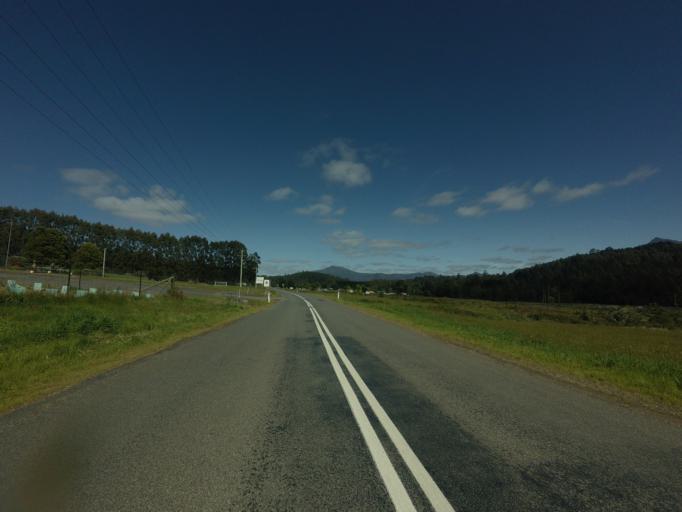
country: AU
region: Tasmania
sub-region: Derwent Valley
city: New Norfolk
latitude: -42.7533
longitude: 146.6333
